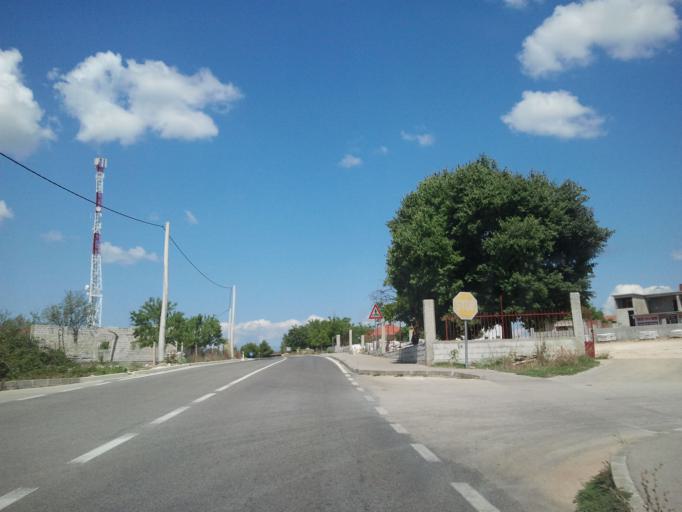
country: HR
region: Zadarska
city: Benkovac
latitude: 44.0423
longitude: 15.6172
